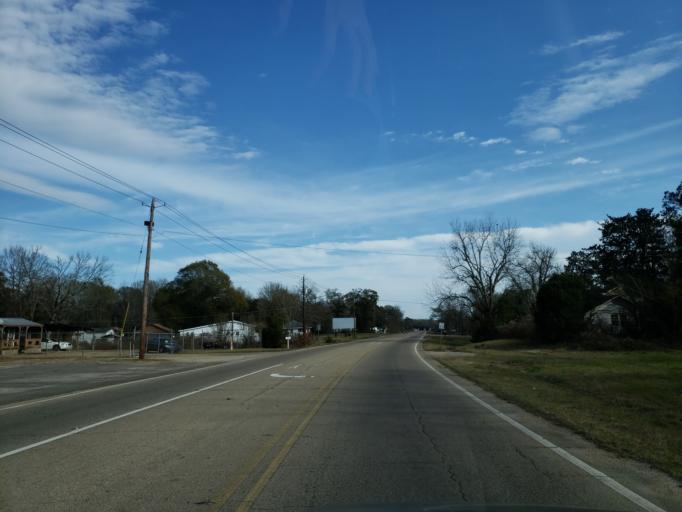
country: US
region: Mississippi
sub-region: Forrest County
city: Hattiesburg
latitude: 31.3434
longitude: -89.2961
